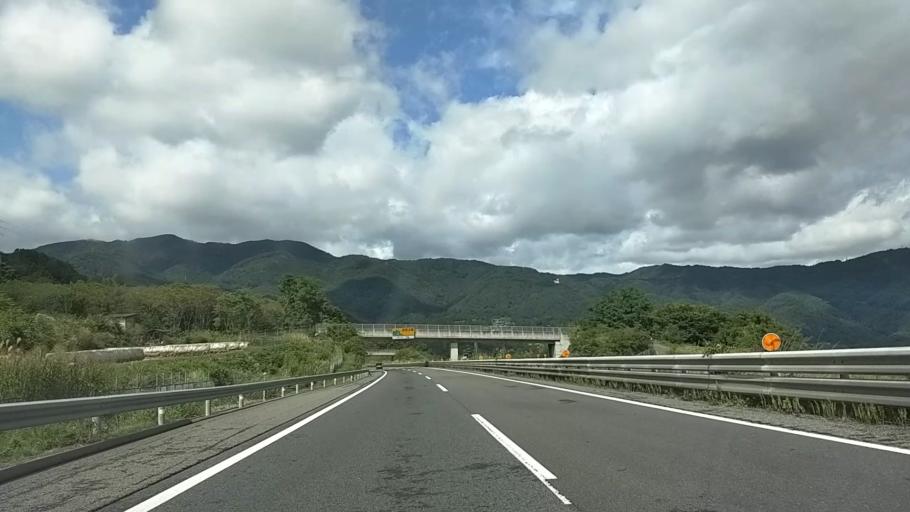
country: JP
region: Nagano
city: Nagano-shi
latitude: 36.5050
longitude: 138.0891
